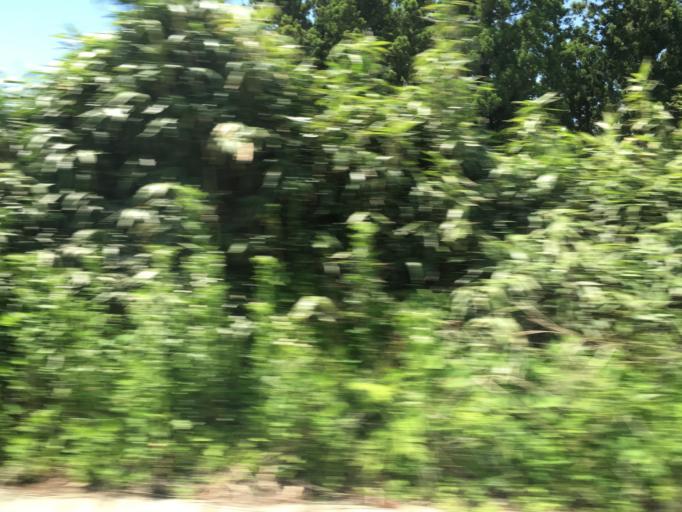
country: JP
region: Fukushima
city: Namie
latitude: 37.5049
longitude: 140.9874
